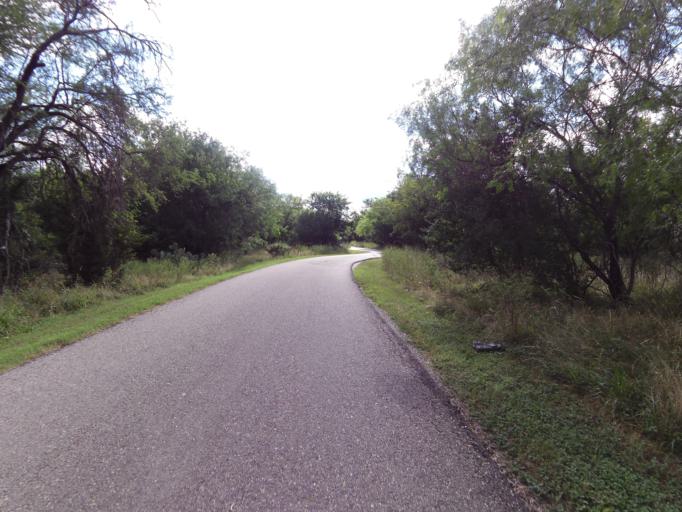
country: US
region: Texas
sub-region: Bexar County
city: Shavano Park
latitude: 29.5754
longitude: -98.6137
